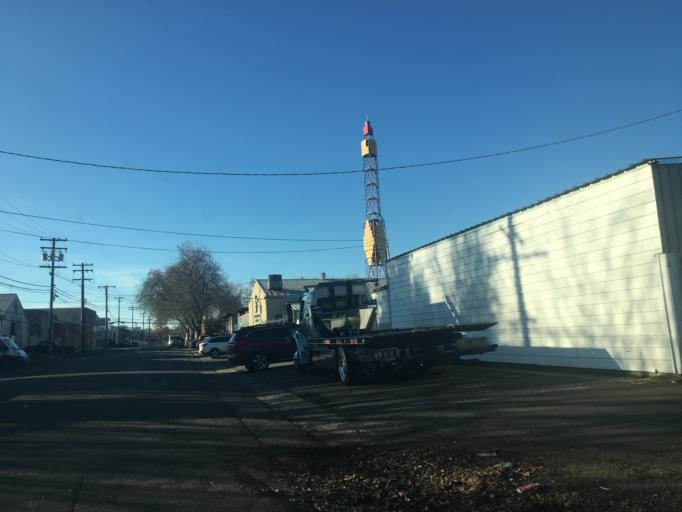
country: US
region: California
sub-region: Sacramento County
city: Sacramento
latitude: 38.5640
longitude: -121.5061
